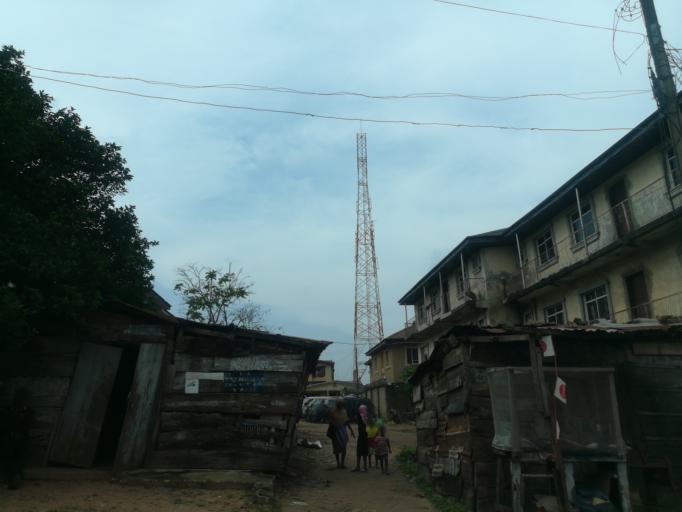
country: NG
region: Oyo
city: Ibadan
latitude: 7.4144
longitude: 3.8984
